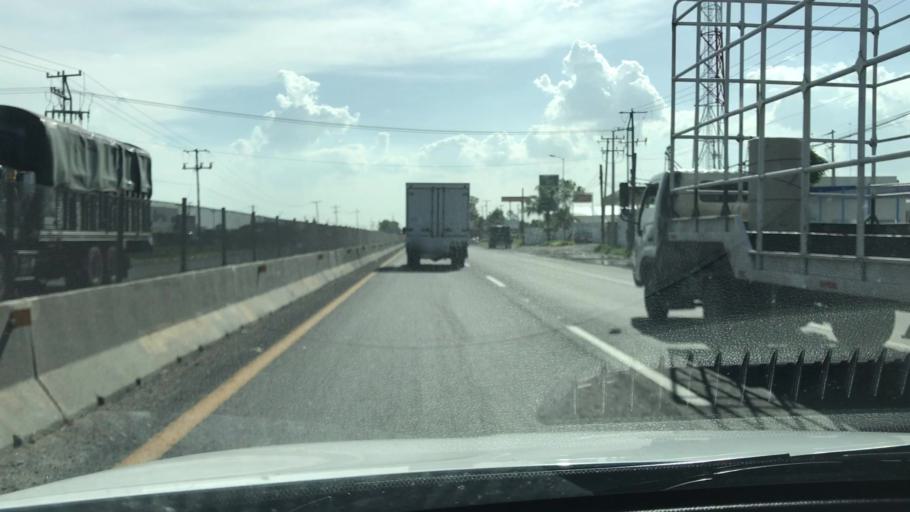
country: MX
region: Guanajuato
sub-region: Villagran
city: El Chinaco (El Pujido)
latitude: 20.5128
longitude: -100.9312
